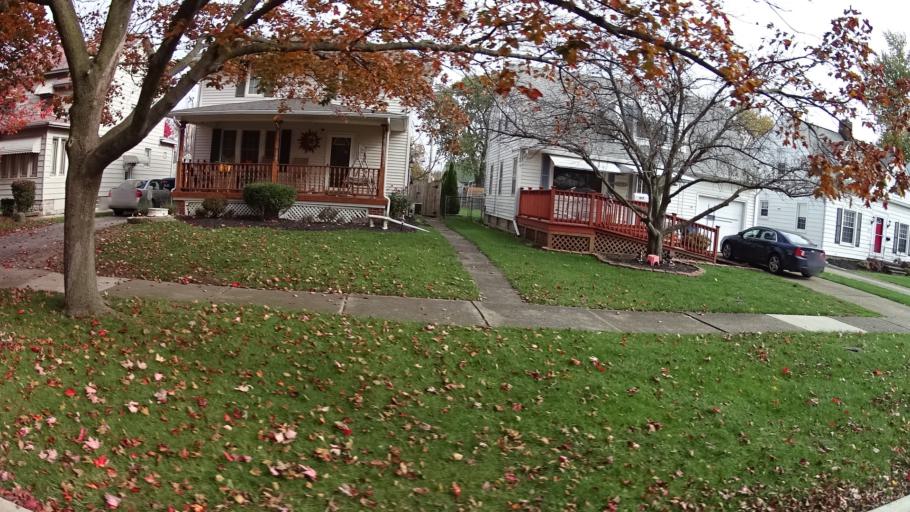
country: US
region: Ohio
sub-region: Lorain County
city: Sheffield Lake
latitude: 41.4793
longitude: -82.1389
